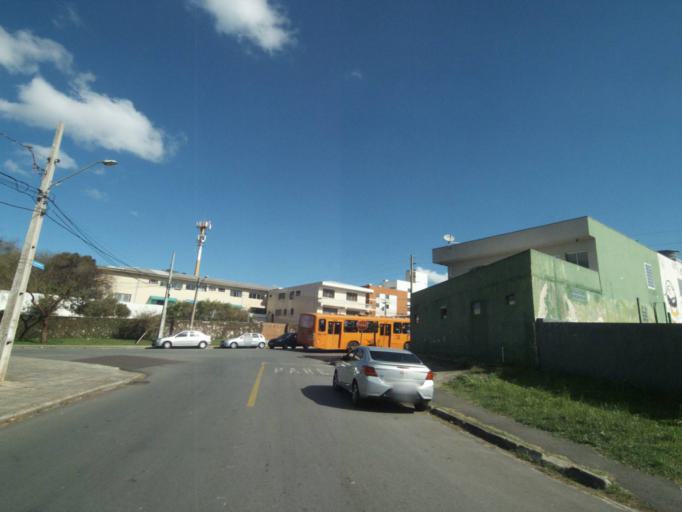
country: BR
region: Parana
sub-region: Curitiba
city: Curitiba
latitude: -25.3845
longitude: -49.2480
